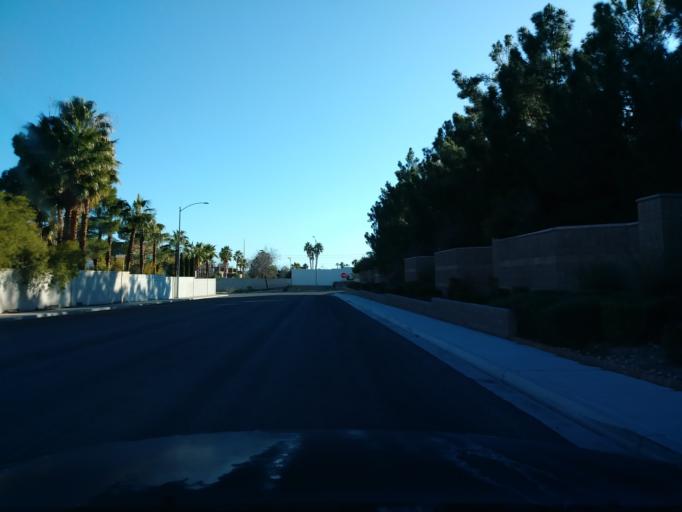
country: US
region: Nevada
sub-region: Clark County
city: Spring Valley
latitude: 36.1465
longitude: -115.2680
